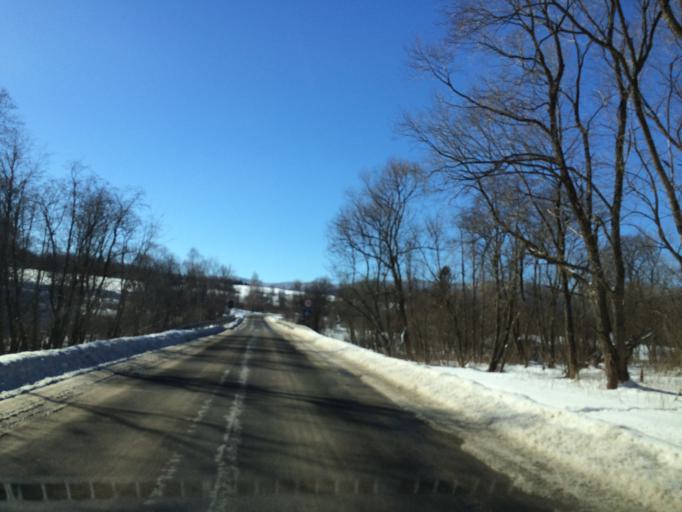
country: PL
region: Subcarpathian Voivodeship
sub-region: Powiat bieszczadzki
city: Lutowiska
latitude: 49.1135
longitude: 22.6620
